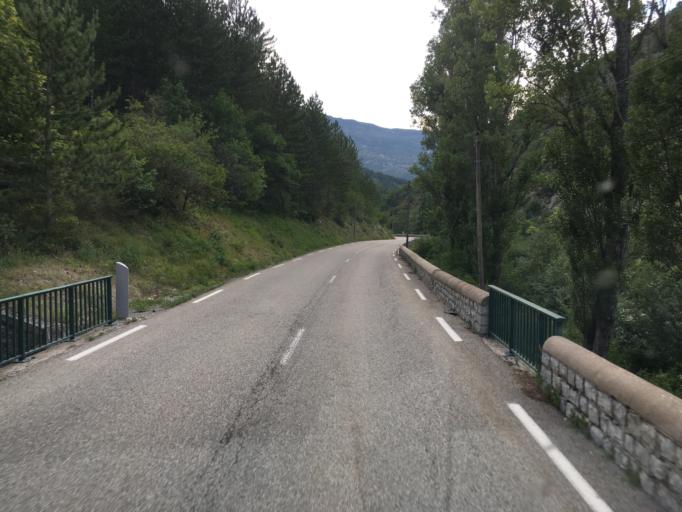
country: FR
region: Rhone-Alpes
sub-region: Departement de la Drome
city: Buis-les-Baronnies
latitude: 44.3895
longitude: 5.3764
